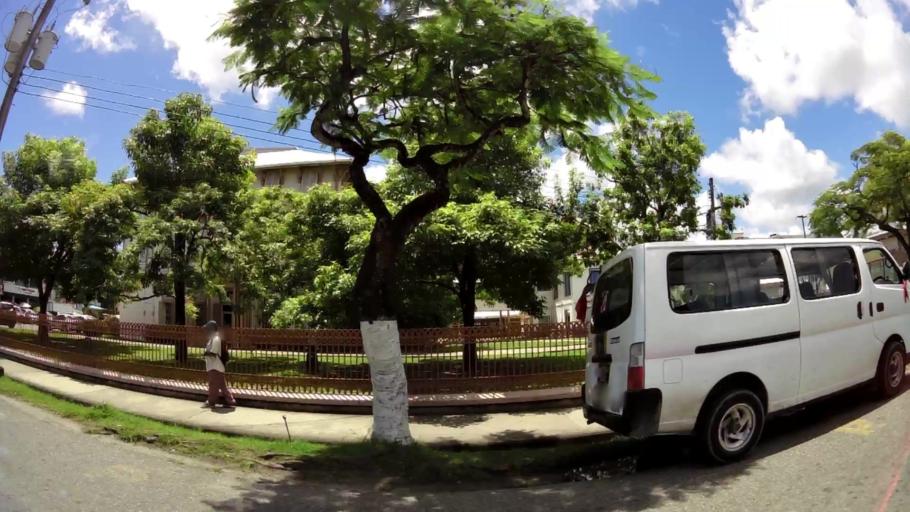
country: GY
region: Demerara-Mahaica
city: Georgetown
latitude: 6.8118
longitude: -58.1651
